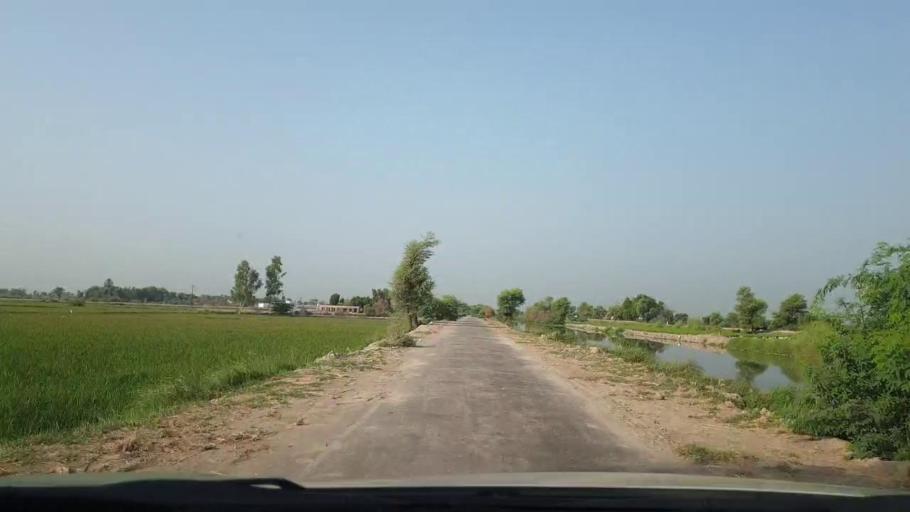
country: PK
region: Sindh
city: Larkana
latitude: 27.4911
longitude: 68.1670
